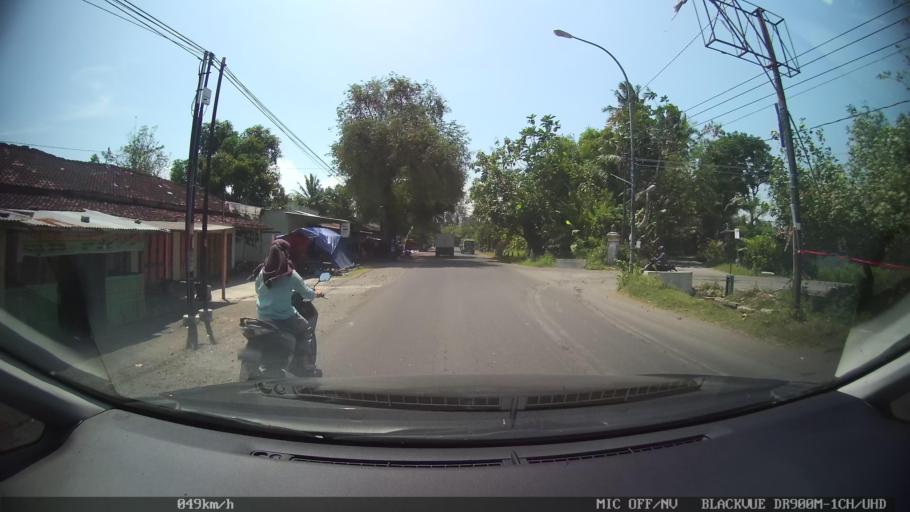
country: ID
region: Daerah Istimewa Yogyakarta
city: Srandakan
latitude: -7.9501
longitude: 110.2187
